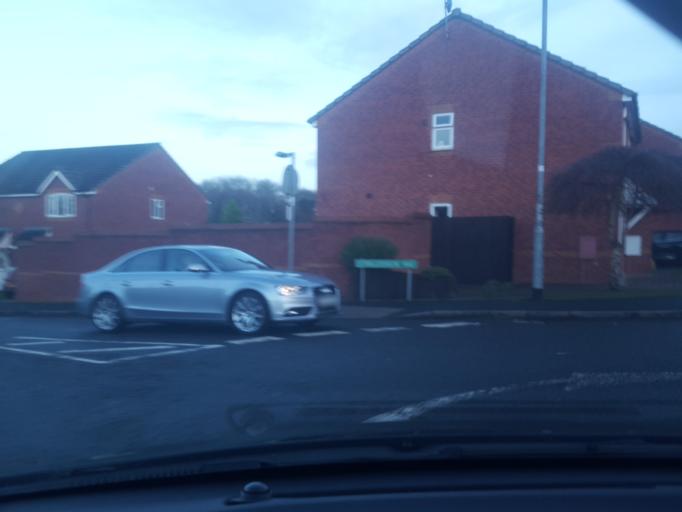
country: GB
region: England
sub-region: Staffordshire
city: Codsall
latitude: 52.6312
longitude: -2.1832
